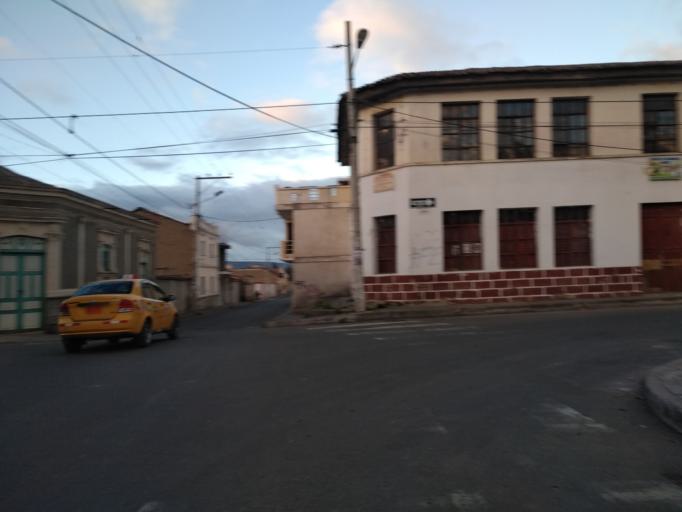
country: EC
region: Chimborazo
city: Riobamba
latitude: -1.6888
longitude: -78.6759
